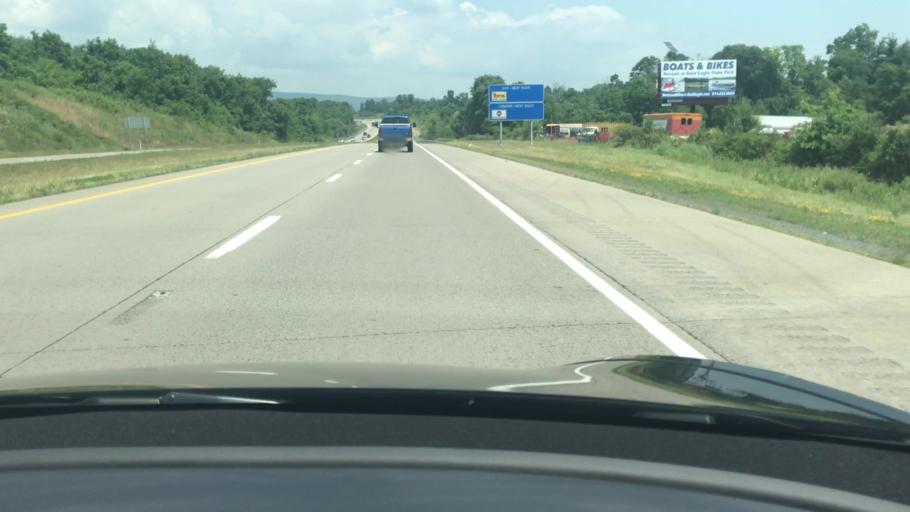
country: US
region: Pennsylvania
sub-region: Mifflin County
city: Church Hill
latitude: 40.6885
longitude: -77.6045
